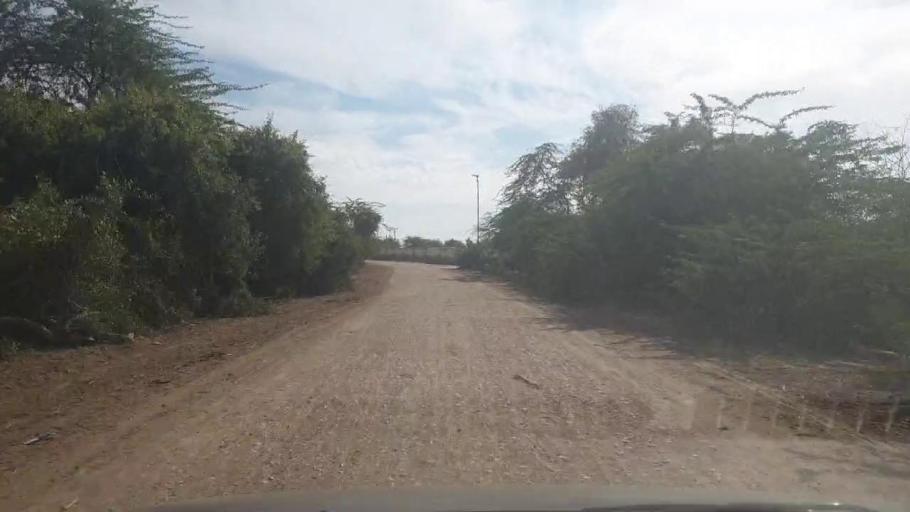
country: PK
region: Sindh
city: Pithoro
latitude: 25.4008
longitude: 69.2510
